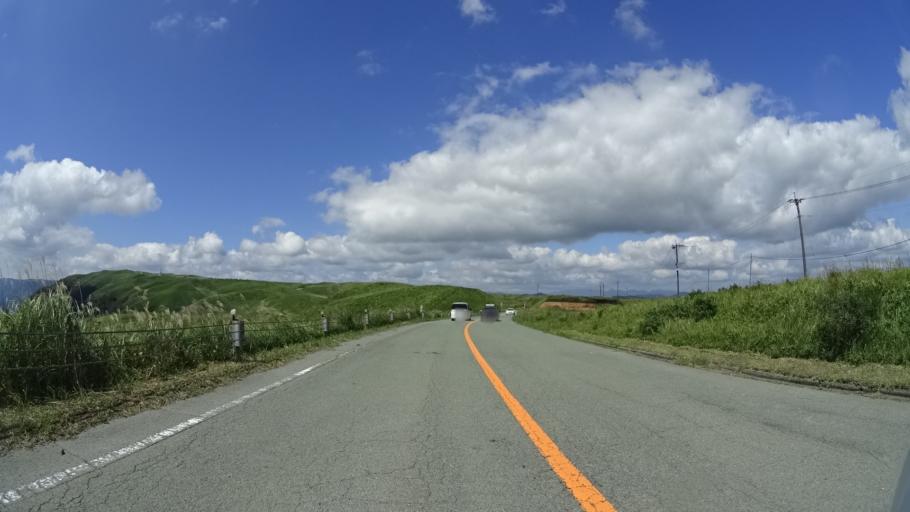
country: JP
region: Kumamoto
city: Aso
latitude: 32.9989
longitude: 131.0820
